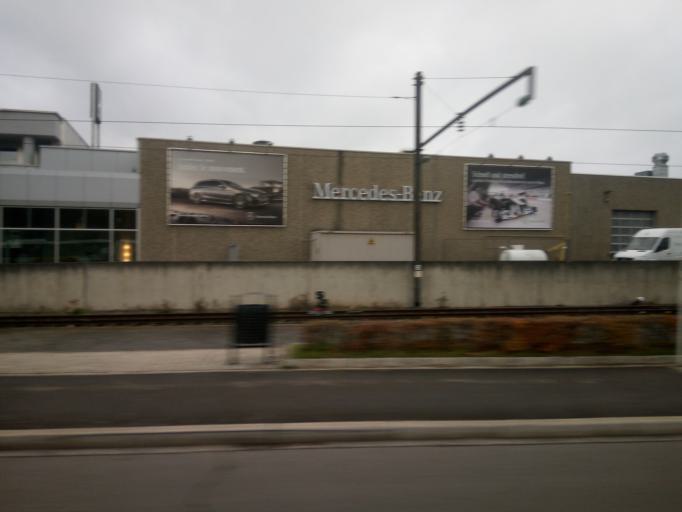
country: LU
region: Diekirch
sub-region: Canton de Diekirch
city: Diekirch
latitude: 49.8644
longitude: 6.1524
